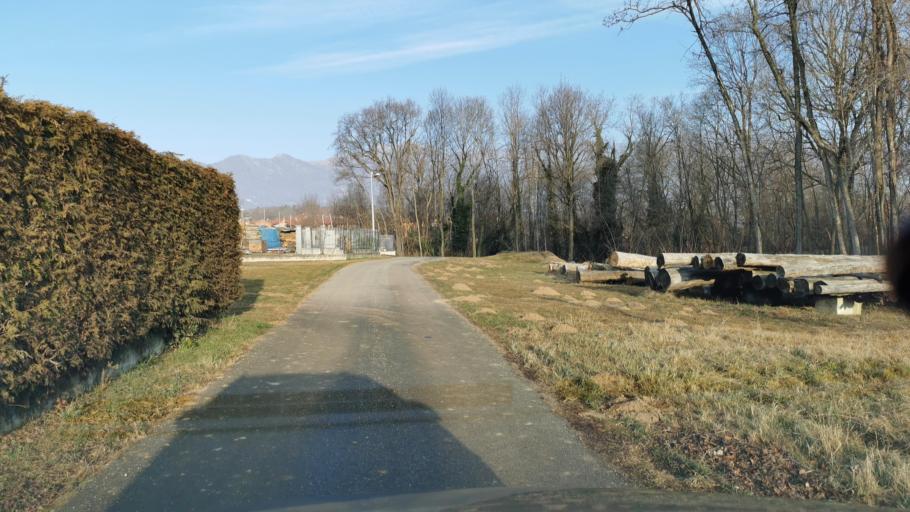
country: IT
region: Piedmont
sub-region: Provincia di Torino
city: Rocca Canavese
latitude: 45.2853
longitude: 7.5752
